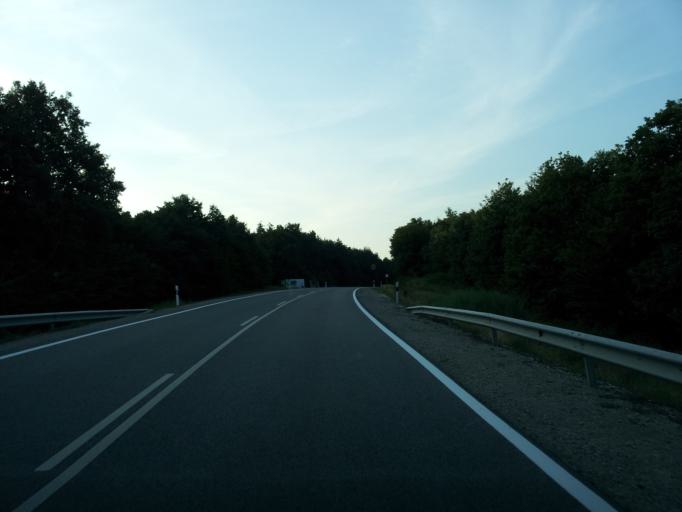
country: HU
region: Zala
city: Zalalovo
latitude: 46.7969
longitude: 16.5635
